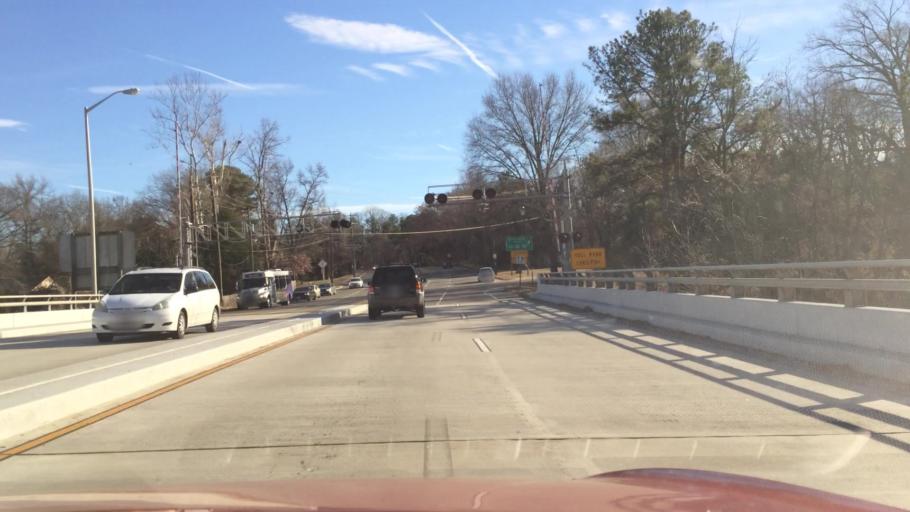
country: US
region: Virginia
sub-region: Chesterfield County
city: Bon Air
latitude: 37.5340
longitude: -77.5079
